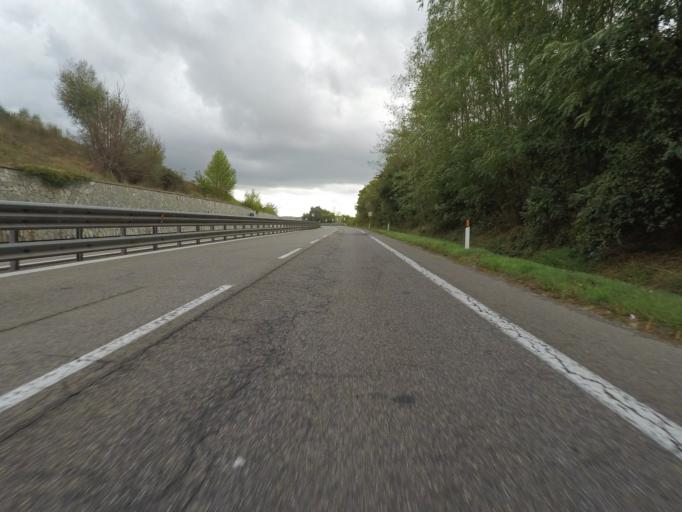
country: IT
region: Tuscany
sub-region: Provincia di Siena
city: Taverne D'Arbia
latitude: 43.2969
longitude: 11.3899
